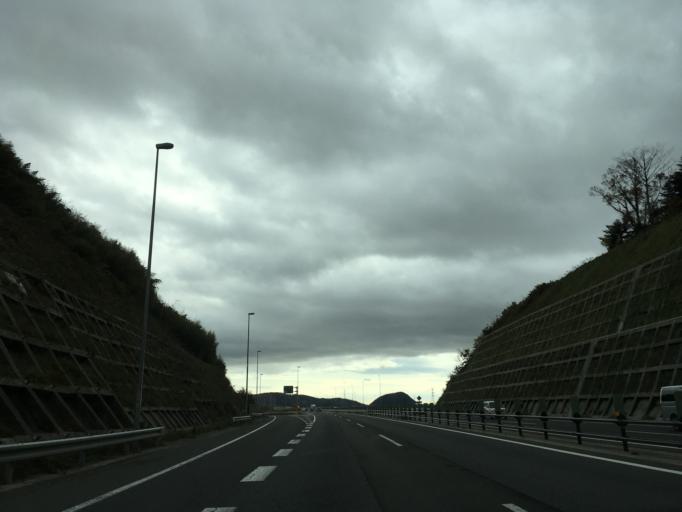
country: JP
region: Miyagi
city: Ishinomaki
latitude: 38.5012
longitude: 141.2866
